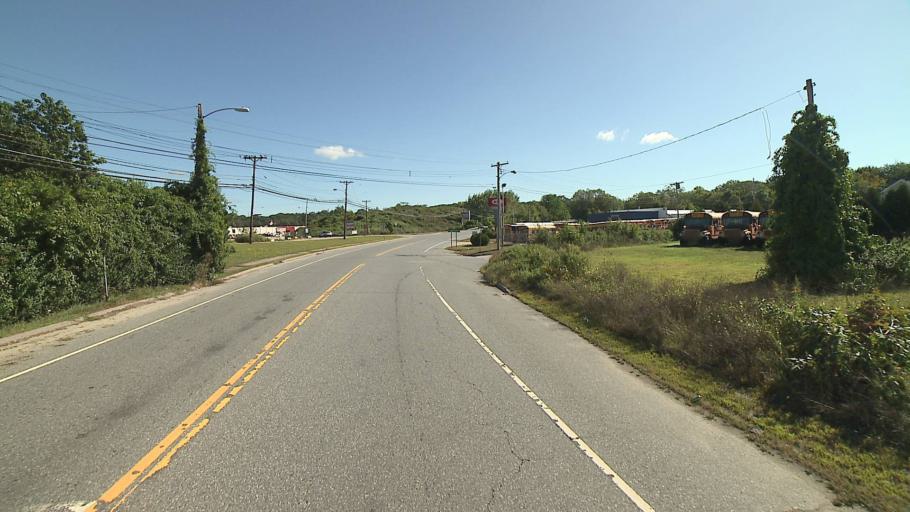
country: US
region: Connecticut
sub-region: New London County
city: Norwich
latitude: 41.5576
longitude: -72.0485
